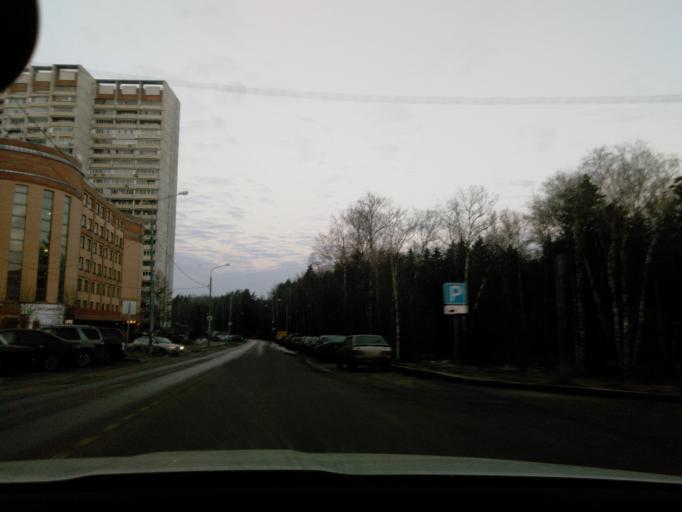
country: RU
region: Moscow
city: Zelenograd
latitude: 55.9997
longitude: 37.1915
